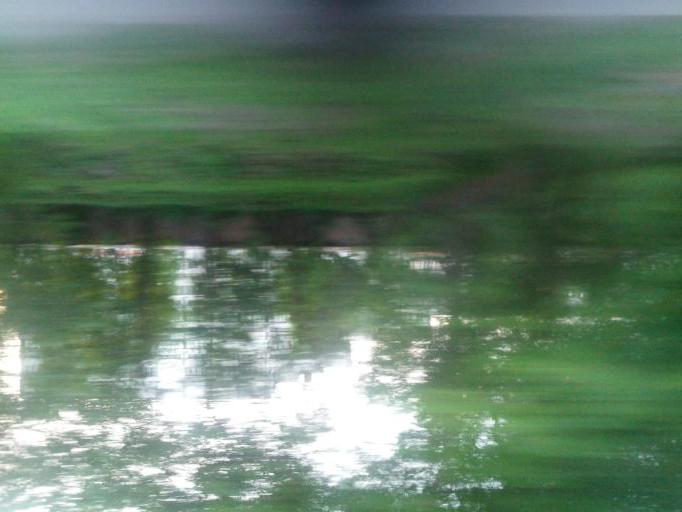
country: RU
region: St.-Petersburg
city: Staraya Derevnya
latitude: 59.9947
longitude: 30.2552
